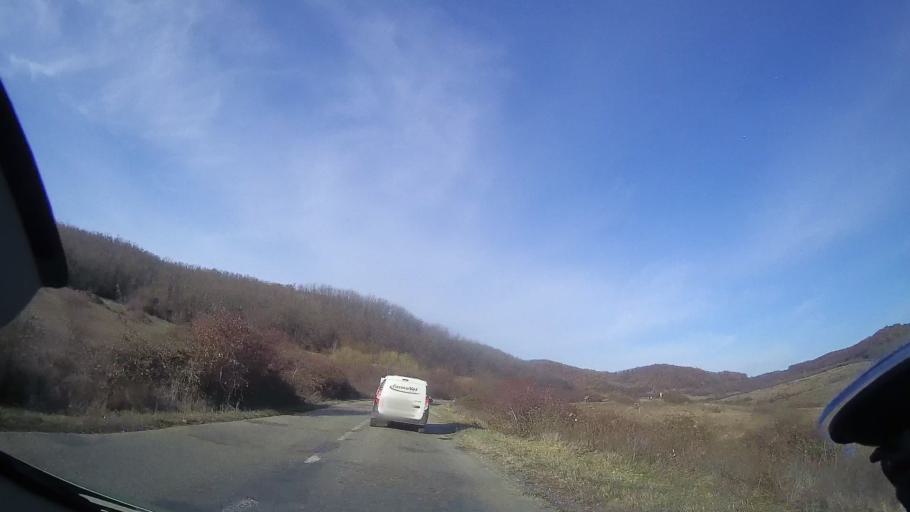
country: RO
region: Bihor
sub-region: Comuna Tileagd
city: Tileagd
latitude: 47.0873
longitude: 22.2347
